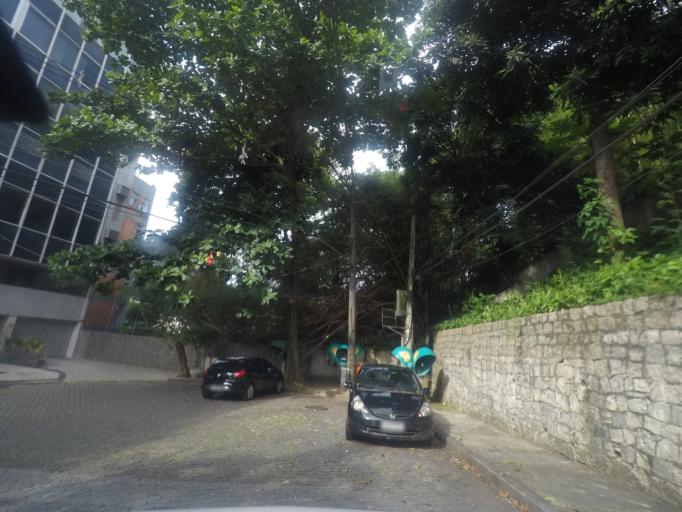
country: BR
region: Rio de Janeiro
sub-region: Rio De Janeiro
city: Rio de Janeiro
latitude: -22.9599
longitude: -43.2002
